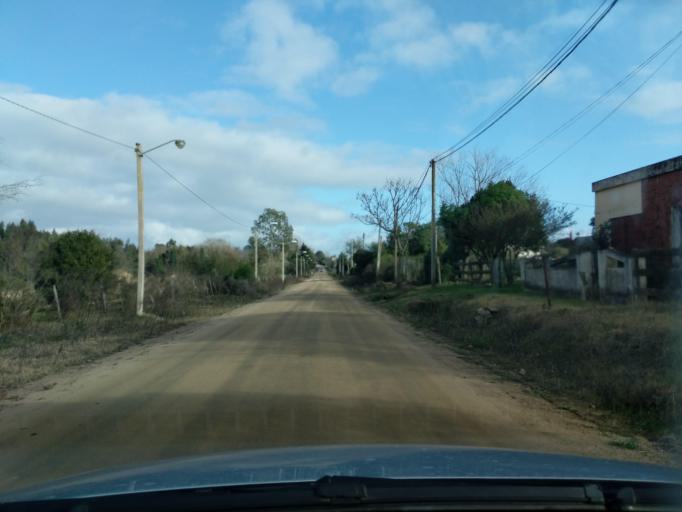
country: UY
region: Florida
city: Florida
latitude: -34.0812
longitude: -56.2066
